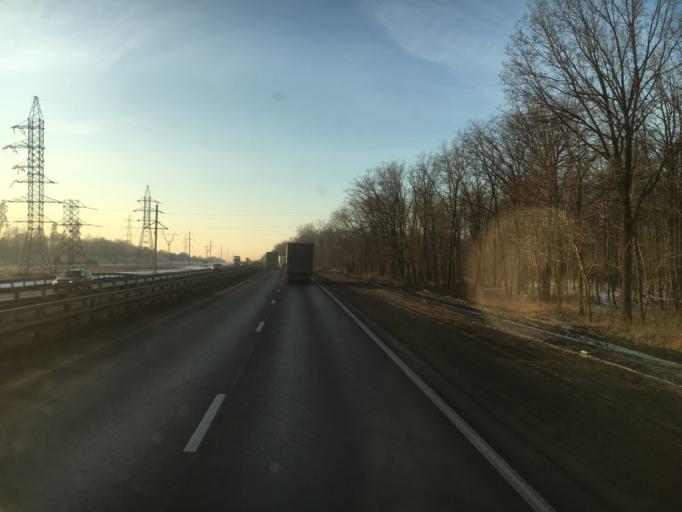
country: RU
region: Samara
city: Pribrezhnyy
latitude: 53.5186
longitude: 49.8195
